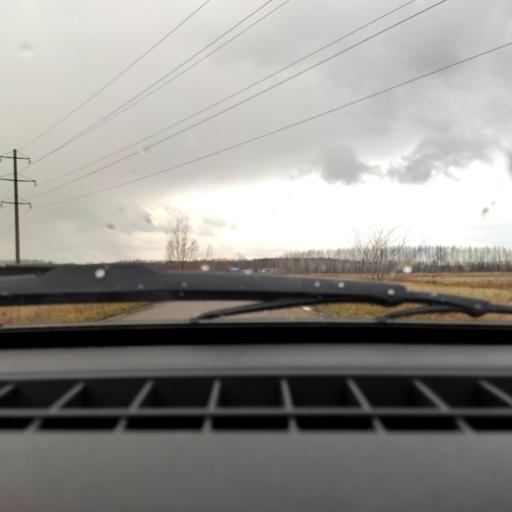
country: RU
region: Bashkortostan
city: Iglino
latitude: 54.7424
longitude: 56.3198
